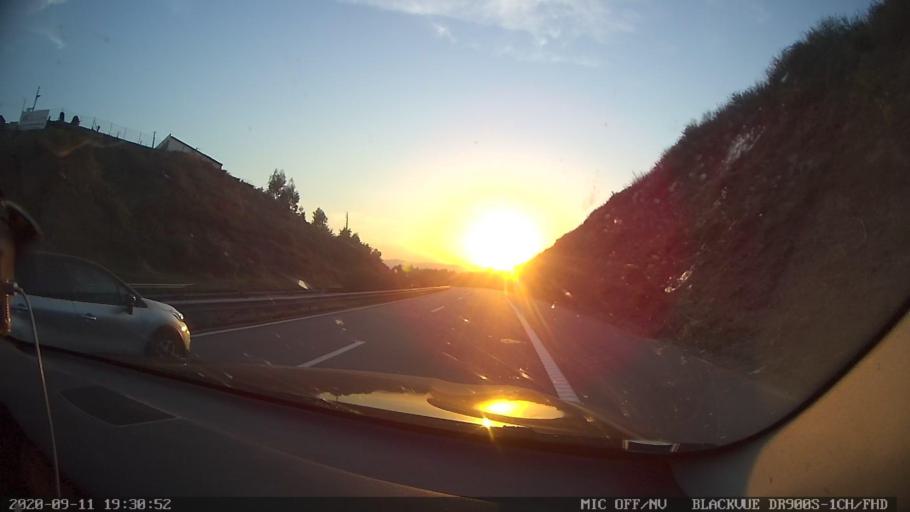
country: PT
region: Porto
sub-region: Penafiel
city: Penafiel
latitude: 41.2210
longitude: -8.2591
